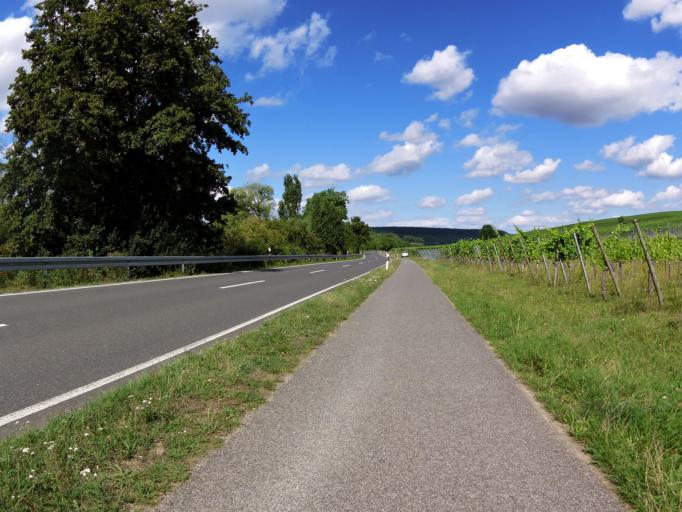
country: DE
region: Bavaria
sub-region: Regierungsbezirk Unterfranken
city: Sommerach
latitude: 49.8339
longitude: 10.1882
